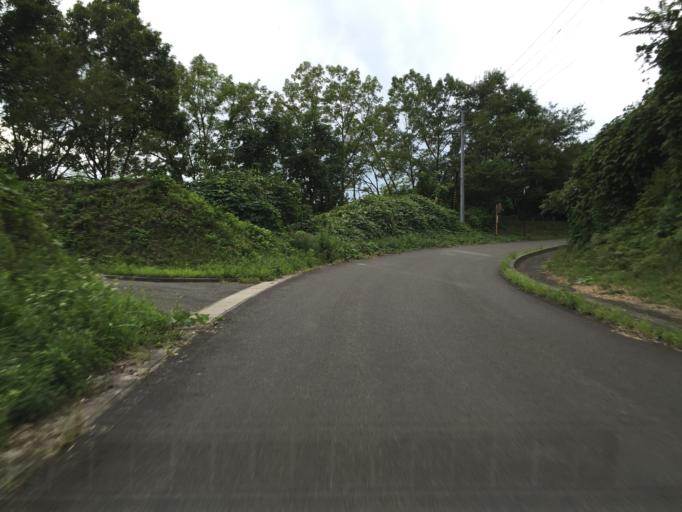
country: JP
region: Fukushima
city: Fukushima-shi
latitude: 37.6682
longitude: 140.5813
